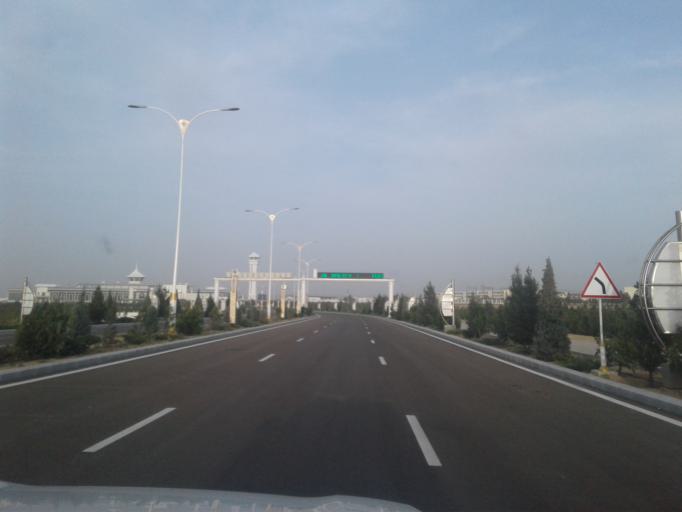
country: TM
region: Balkan
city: Turkmenbasy
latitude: 40.0438
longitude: 52.9848
